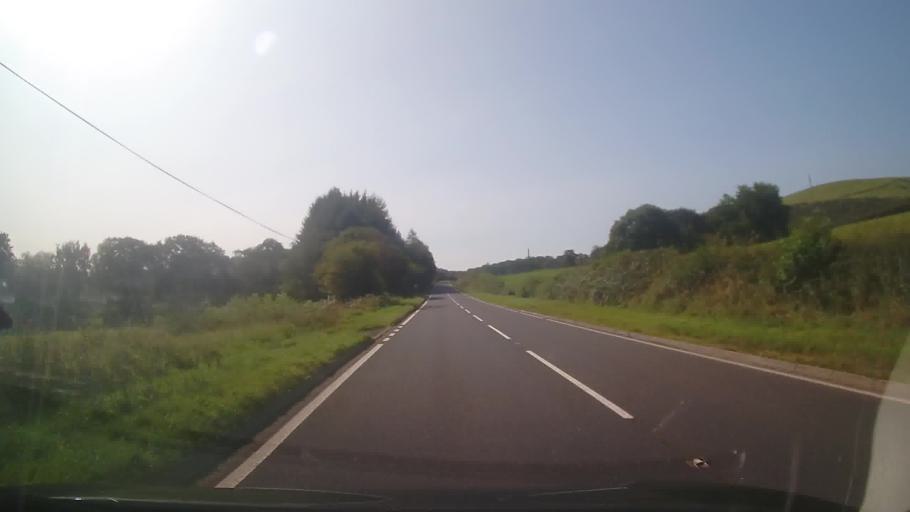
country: GB
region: Wales
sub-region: Sir Powys
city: Rhayader
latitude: 52.1306
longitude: -3.6132
